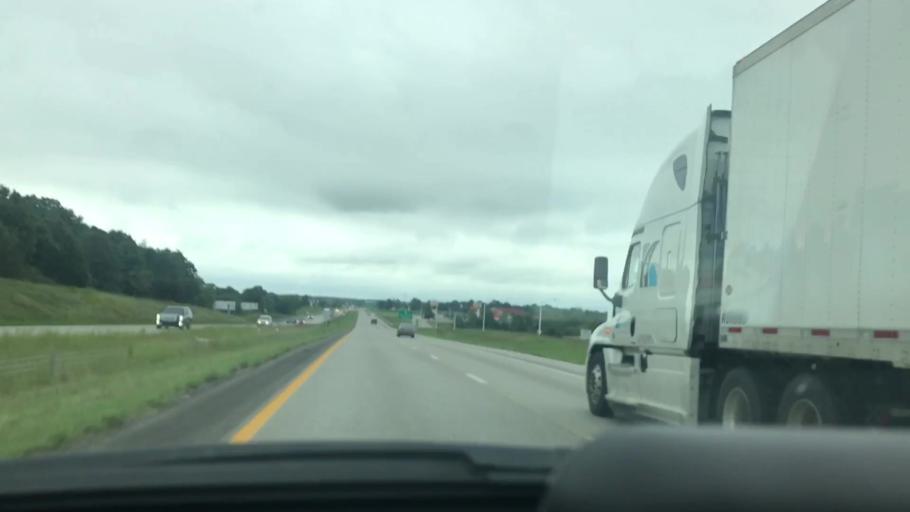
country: US
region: Missouri
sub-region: Jasper County
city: Joplin
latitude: 37.0458
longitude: -94.4916
